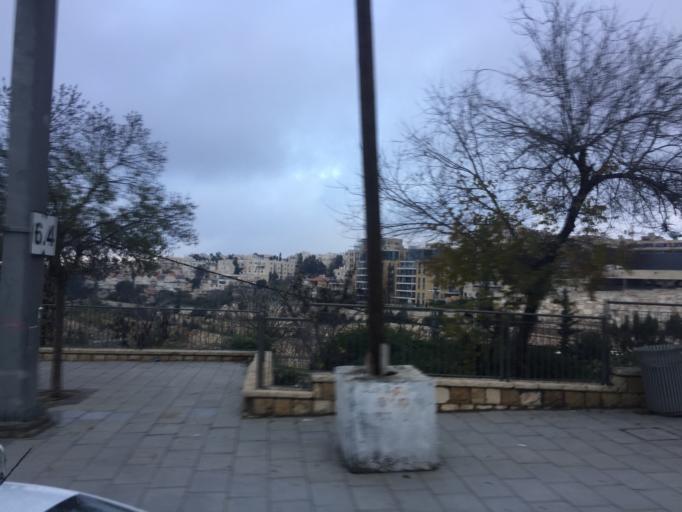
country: IL
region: Jerusalem
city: West Jerusalem
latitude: 31.7908
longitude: 35.1974
